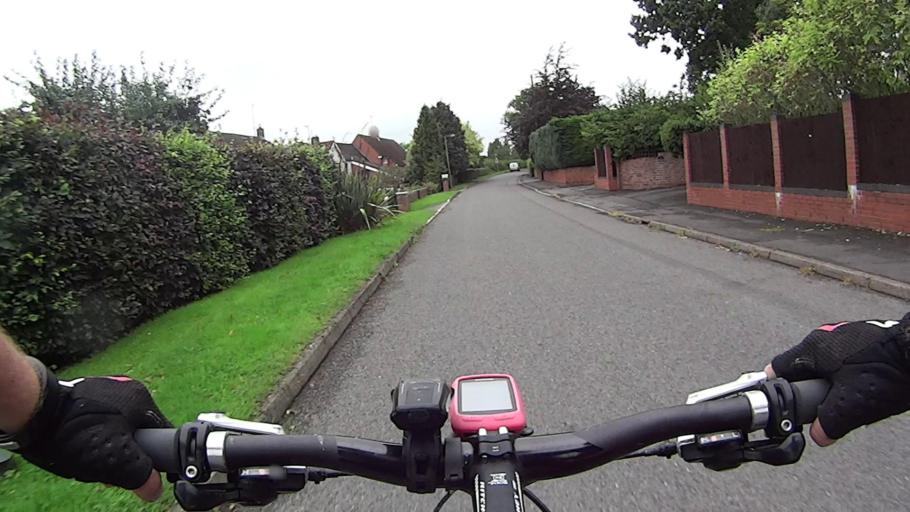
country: GB
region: England
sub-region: Worcestershire
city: Tenbury Wells
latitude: 52.3054
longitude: -2.6044
